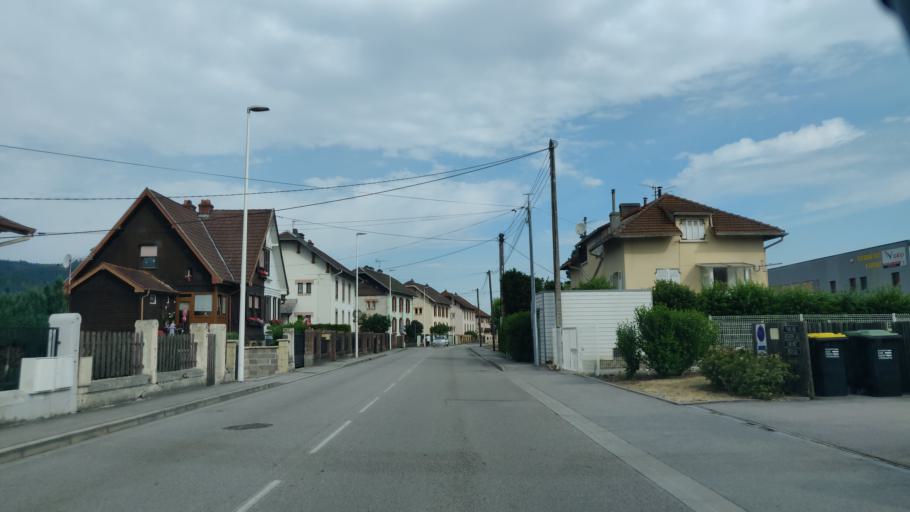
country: FR
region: Lorraine
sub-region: Departement des Vosges
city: Saint-Die-des-Vosges
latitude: 48.2877
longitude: 6.9398
